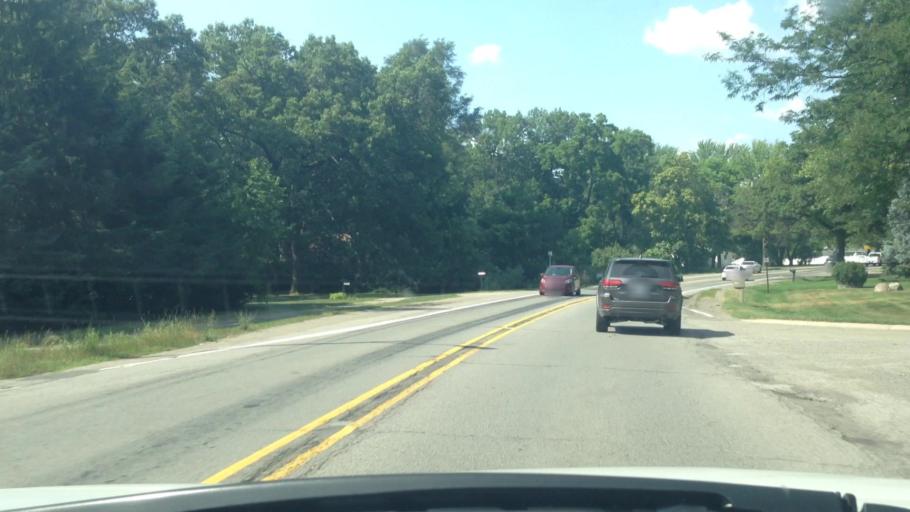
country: US
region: Michigan
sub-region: Oakland County
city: Waterford
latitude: 42.6944
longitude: -83.3729
